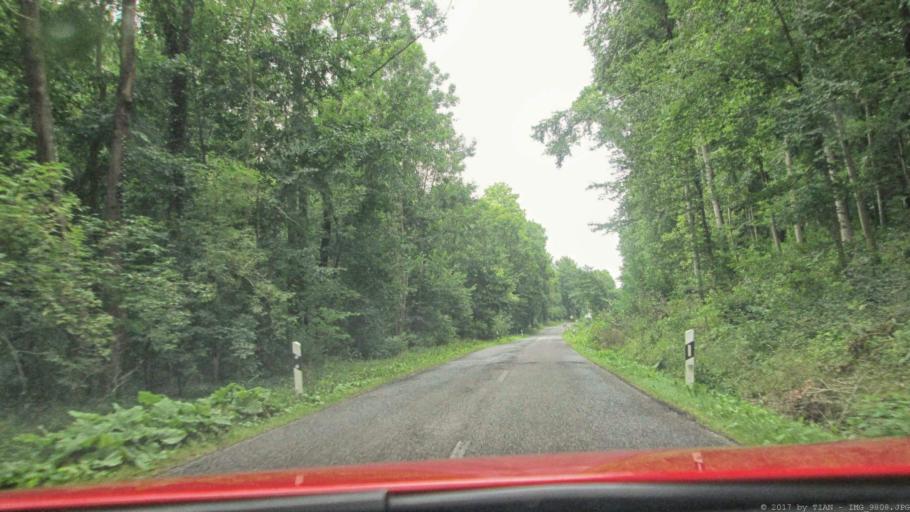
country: DE
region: Hesse
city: Witzenhausen
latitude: 51.4011
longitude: 9.8321
